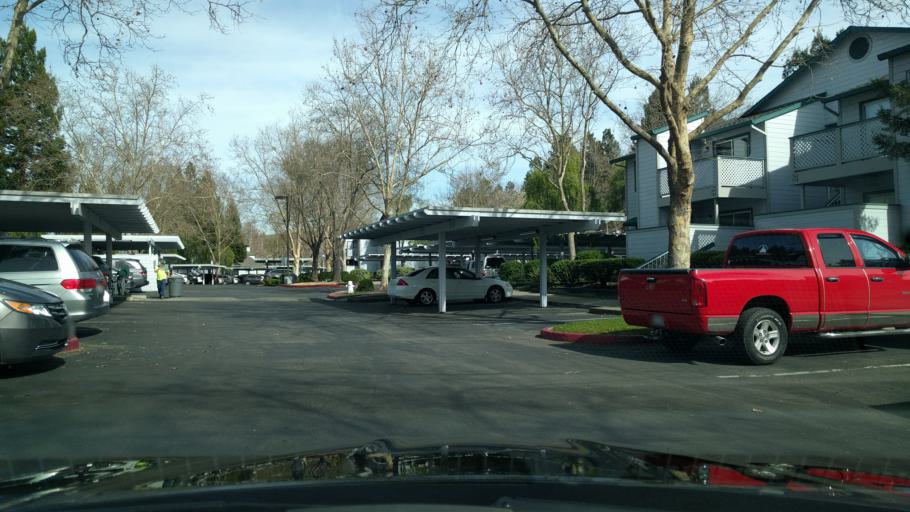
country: US
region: California
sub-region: Contra Costa County
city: San Ramon
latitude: 37.7581
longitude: -121.9464
